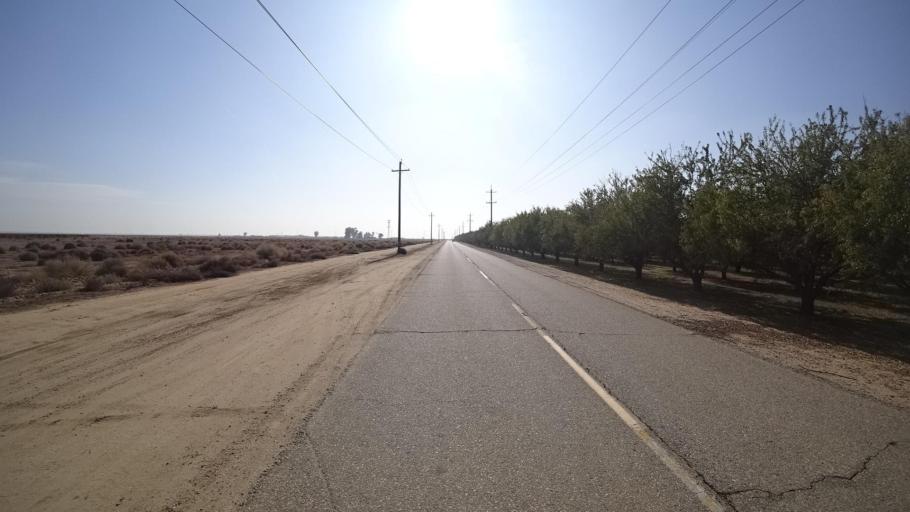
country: US
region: California
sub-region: Kern County
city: Rosedale
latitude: 35.4969
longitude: -119.1526
